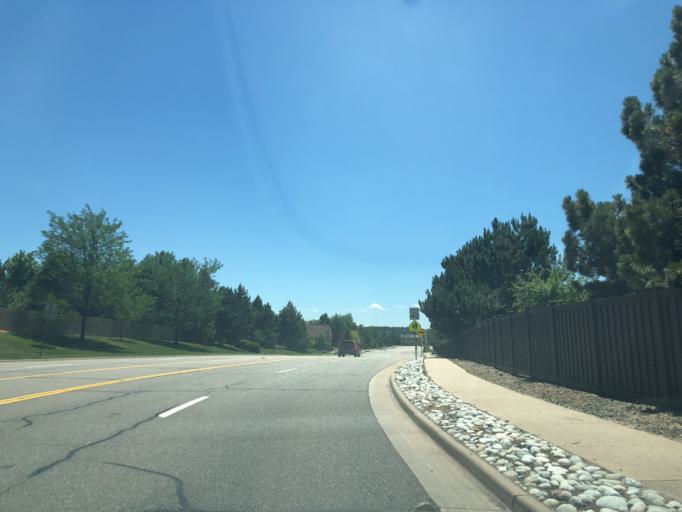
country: US
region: Colorado
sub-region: Arapahoe County
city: Dove Valley
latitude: 39.6168
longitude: -104.7730
